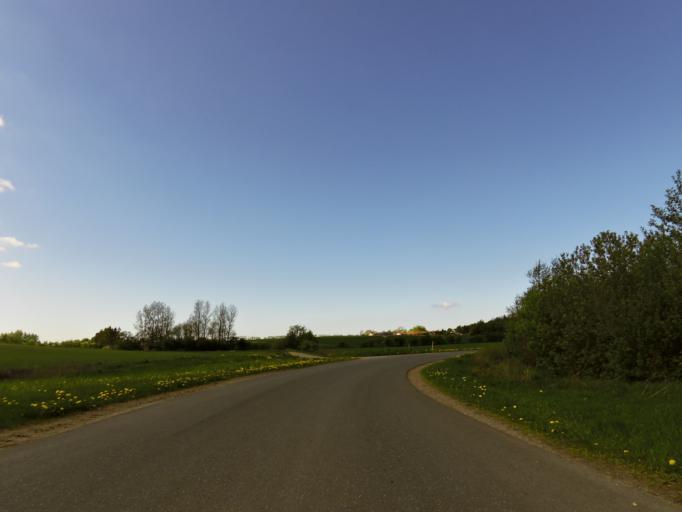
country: DK
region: Central Jutland
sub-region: Holstebro Kommune
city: Vinderup
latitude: 56.4280
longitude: 8.7790
